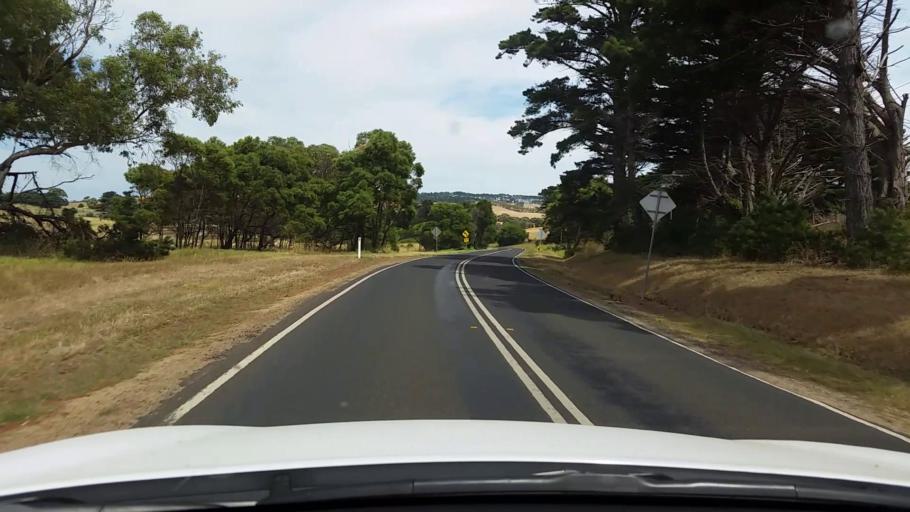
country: AU
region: Victoria
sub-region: Mornington Peninsula
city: Merricks
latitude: -38.4730
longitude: 145.0022
